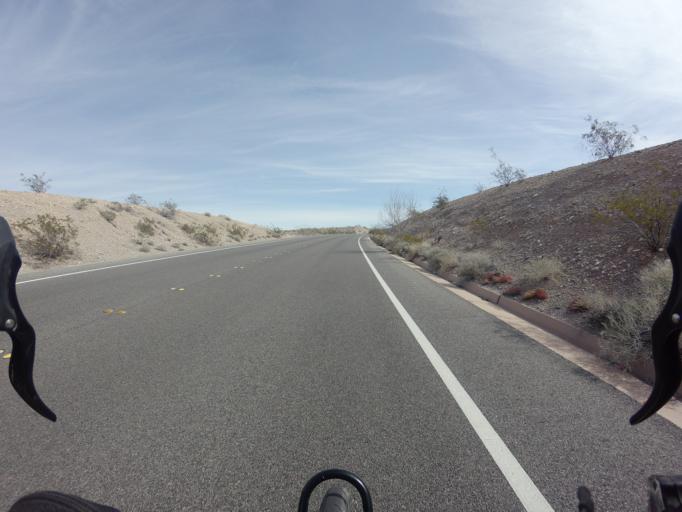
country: US
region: Nevada
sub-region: Clark County
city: Henderson
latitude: 36.1464
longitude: -114.8545
